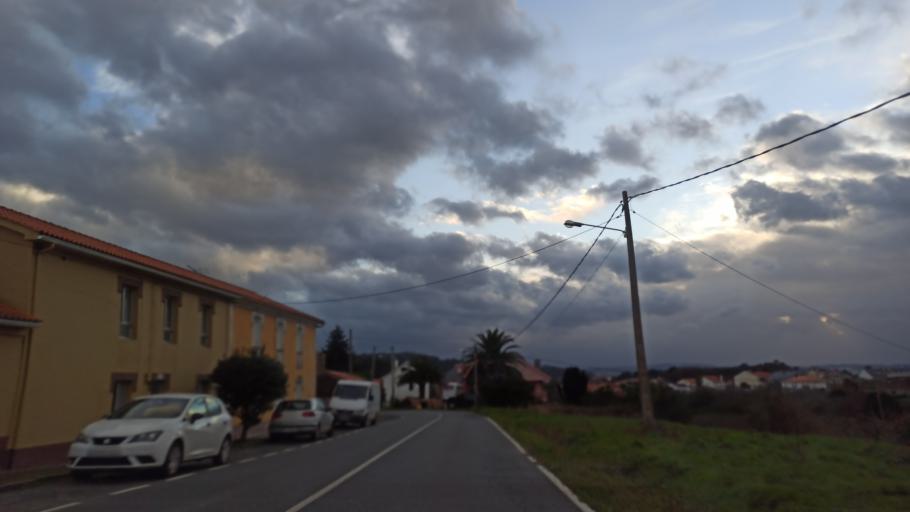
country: ES
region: Galicia
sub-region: Provincia da Coruna
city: Oleiros
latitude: 43.3844
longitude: -8.3221
